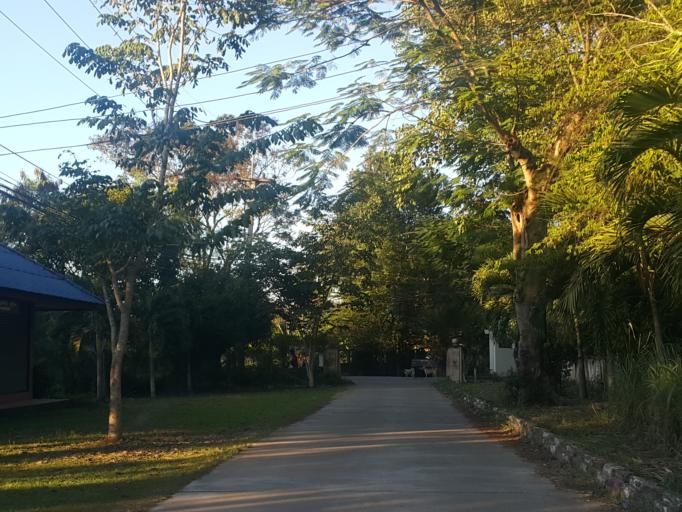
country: TH
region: Chiang Mai
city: San Sai
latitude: 18.8736
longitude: 99.1523
